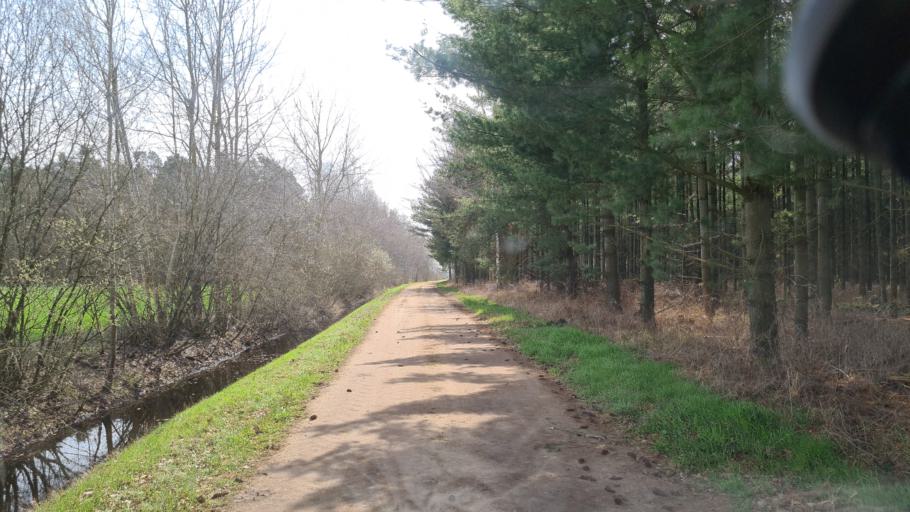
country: DE
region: Brandenburg
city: Bronkow
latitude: 51.6149
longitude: 13.9248
